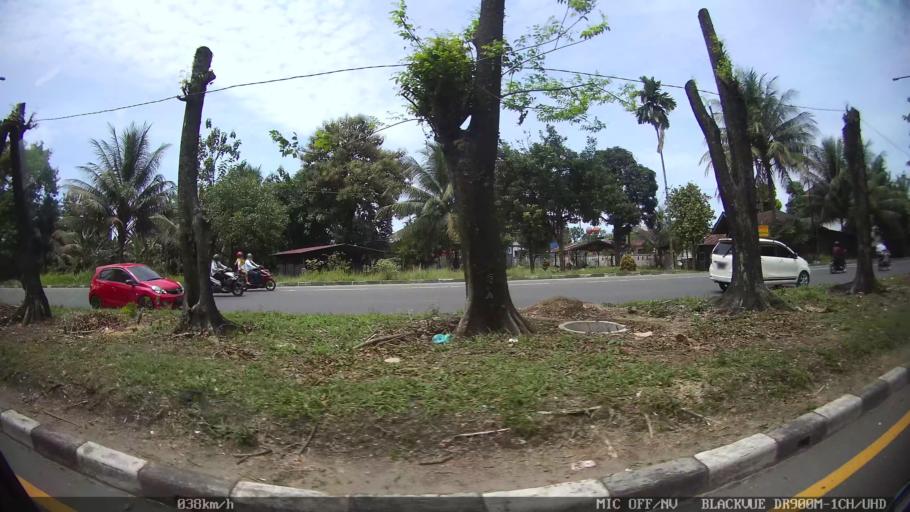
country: ID
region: North Sumatra
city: Sunggal
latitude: 3.5425
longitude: 98.6281
